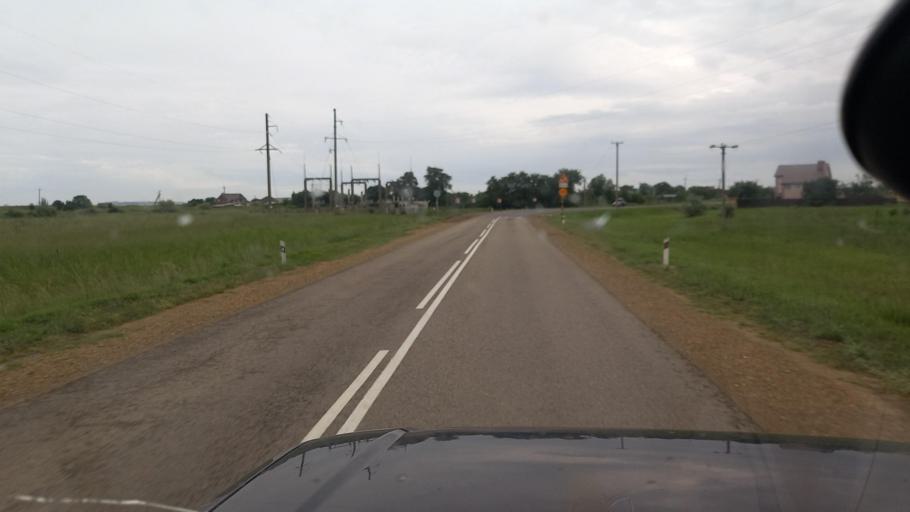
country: RU
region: Krasnodarskiy
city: Akhtanizovskaya
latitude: 45.3358
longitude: 37.1194
